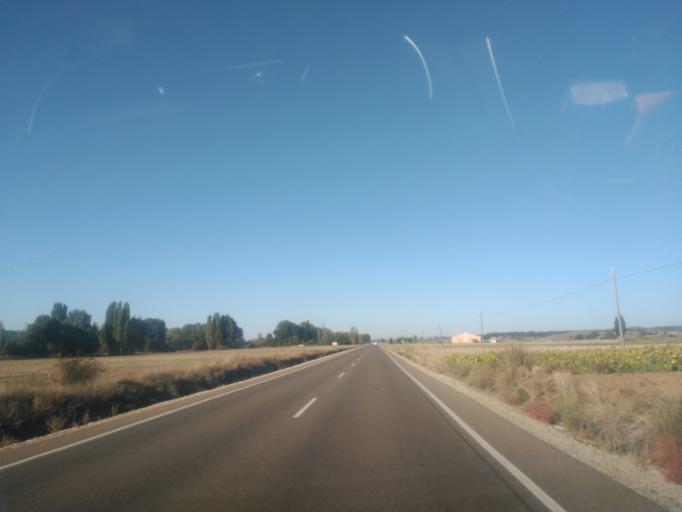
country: ES
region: Castille and Leon
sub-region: Provincia de Burgos
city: Quemada
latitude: 41.6909
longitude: -3.6010
